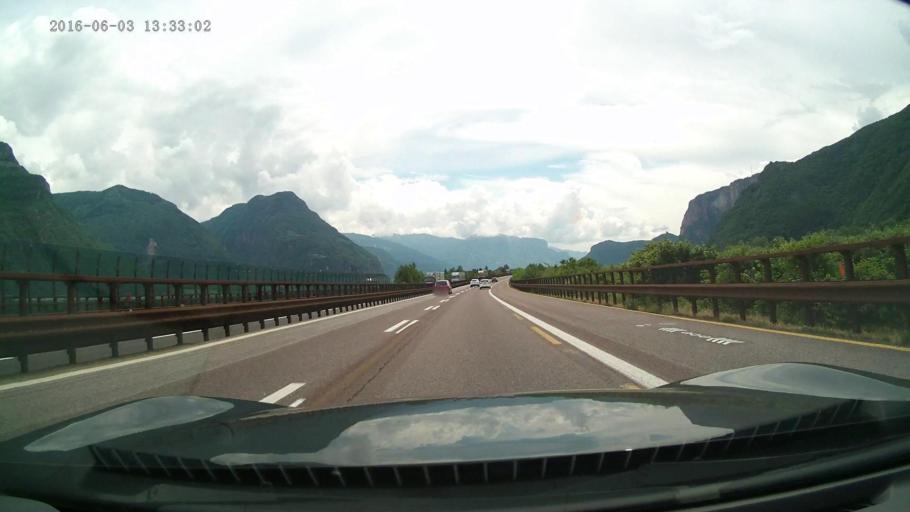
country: IT
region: Trentino-Alto Adige
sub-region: Bolzano
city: Vadena
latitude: 46.4256
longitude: 11.3154
